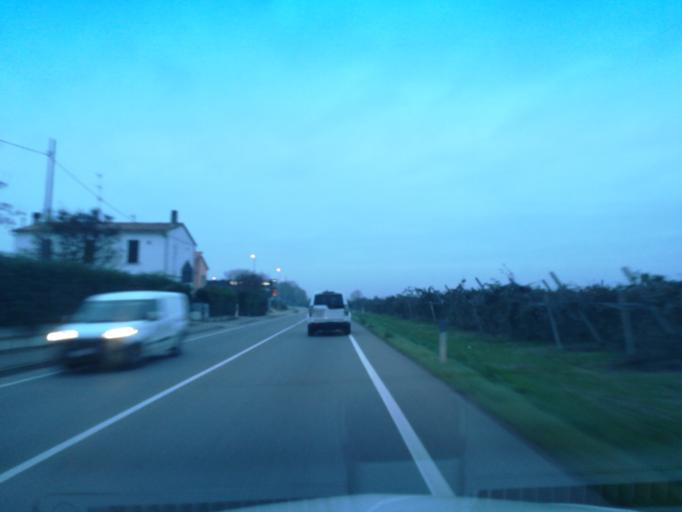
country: IT
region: Emilia-Romagna
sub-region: Provincia di Ravenna
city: Castel Bolognese
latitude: 44.3118
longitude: 11.8215
